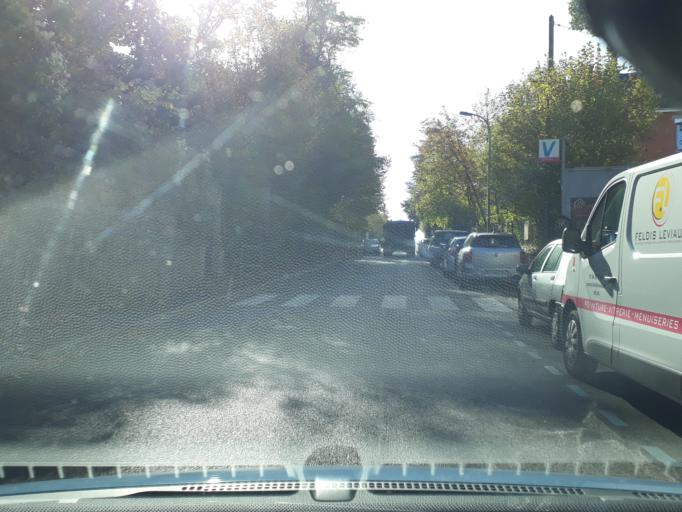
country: FR
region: Ile-de-France
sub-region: Departement de Seine-et-Marne
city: Bois-le-Roi
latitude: 48.4742
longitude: 2.6929
